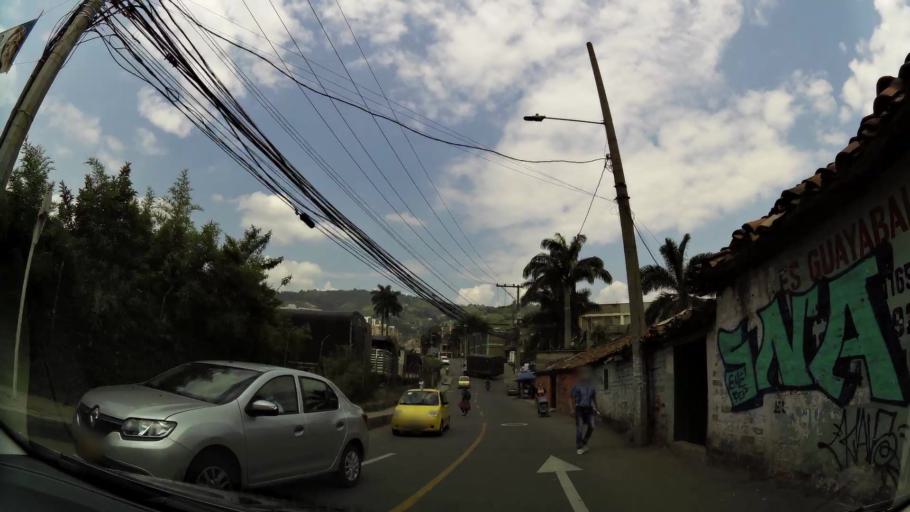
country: CO
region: Antioquia
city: Itagui
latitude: 6.1876
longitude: -75.5977
